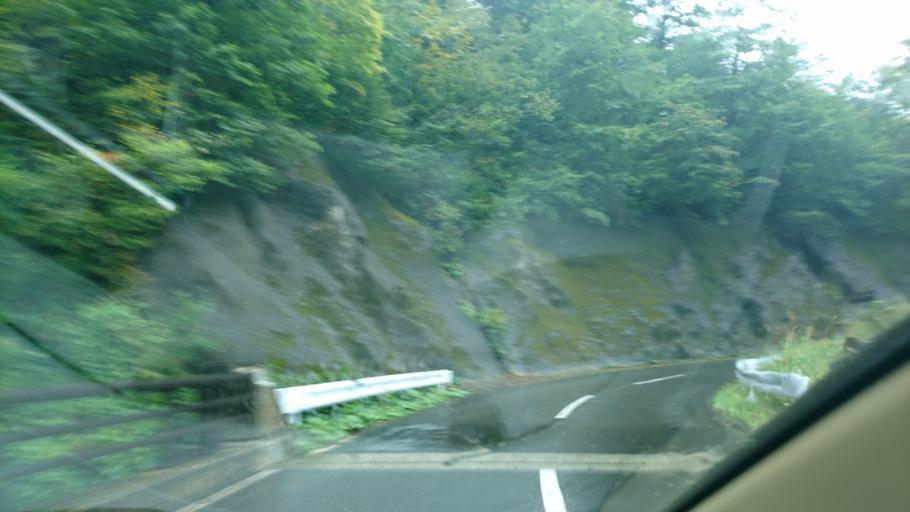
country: JP
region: Iwate
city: Mizusawa
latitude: 39.1291
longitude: 140.8229
